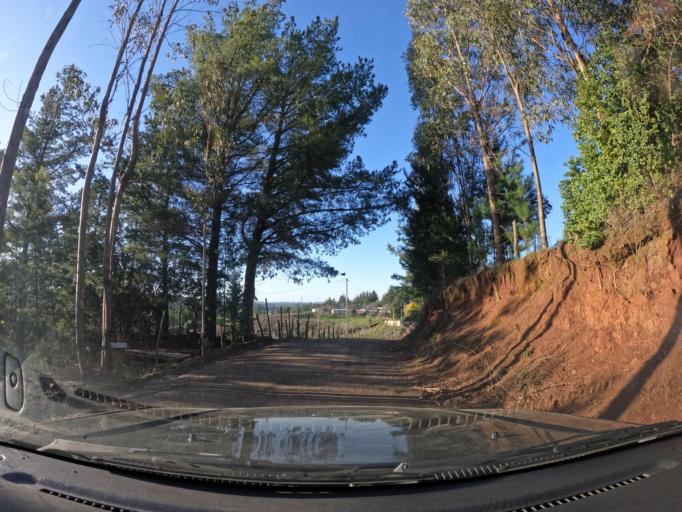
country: CL
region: Biobio
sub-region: Provincia de Concepcion
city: Chiguayante
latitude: -37.0155
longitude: -72.8494
